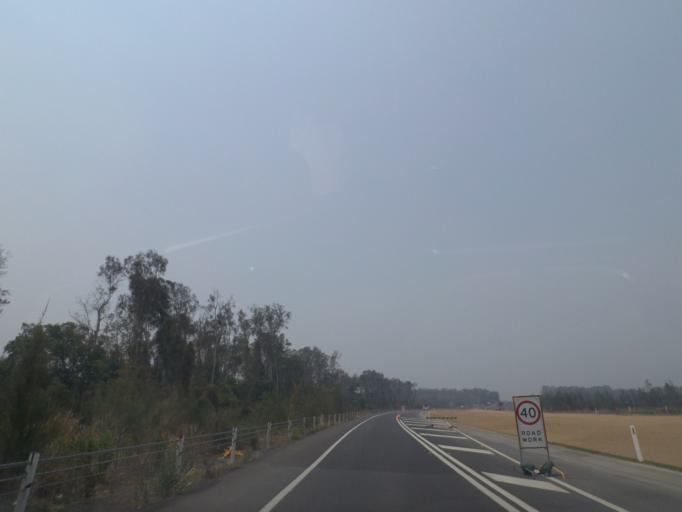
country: AU
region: New South Wales
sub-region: Ballina
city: Ballina
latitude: -28.8684
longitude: 153.4928
